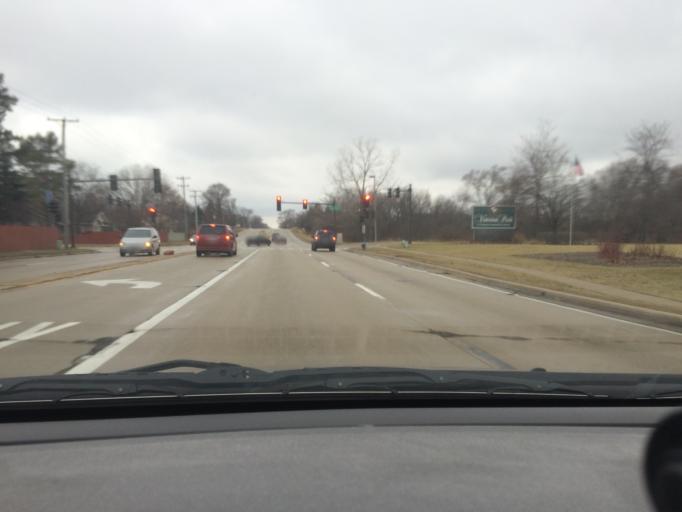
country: US
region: Illinois
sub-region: Cook County
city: Streamwood
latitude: 42.0319
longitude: -88.1644
